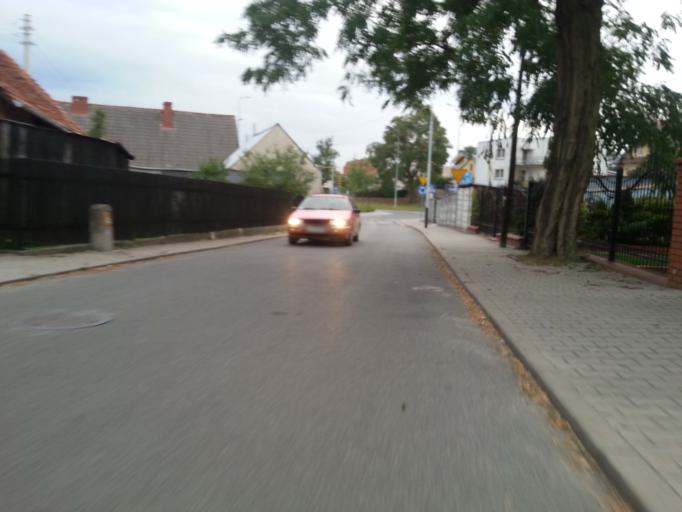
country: PL
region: Lower Silesian Voivodeship
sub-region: Powiat olesnicki
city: Twardogora
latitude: 51.3679
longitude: 17.4617
